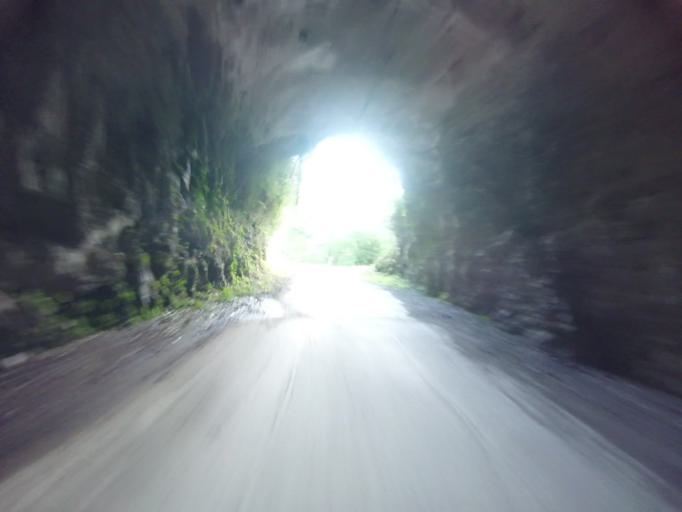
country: ES
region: Basque Country
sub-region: Provincia de Guipuzcoa
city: Berastegui
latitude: 43.1534
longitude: -1.9641
